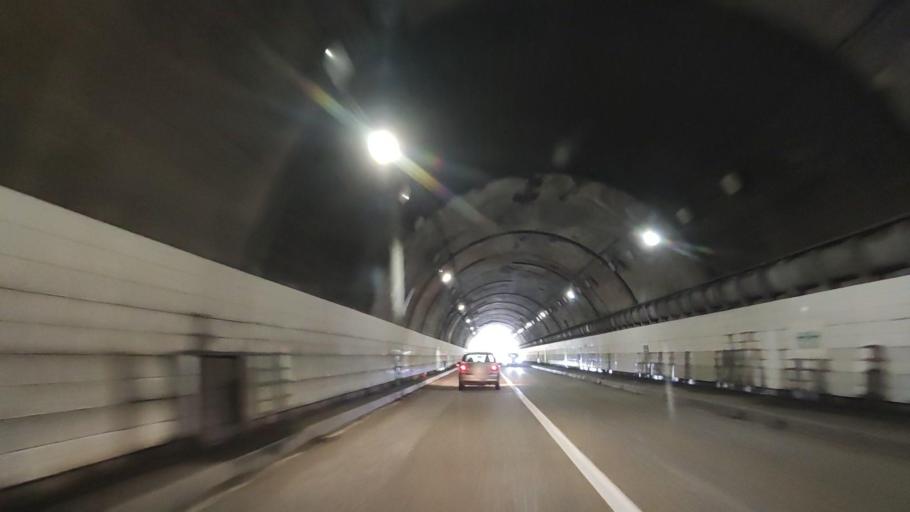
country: JP
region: Akita
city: Takanosu
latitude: 40.2174
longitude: 140.2346
